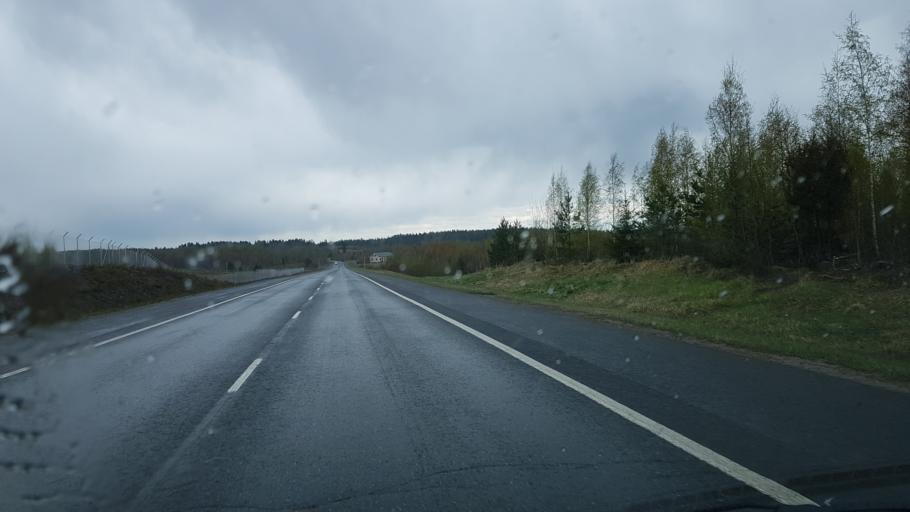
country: FI
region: Pirkanmaa
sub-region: Tampere
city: Pirkkala
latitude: 61.4173
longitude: 23.6344
